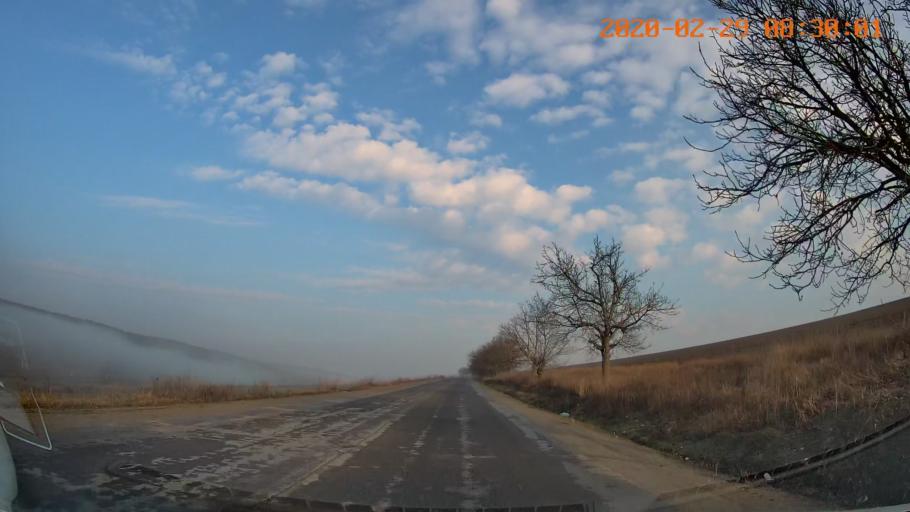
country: MD
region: Anenii Noi
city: Anenii Noi
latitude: 46.8981
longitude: 29.2976
